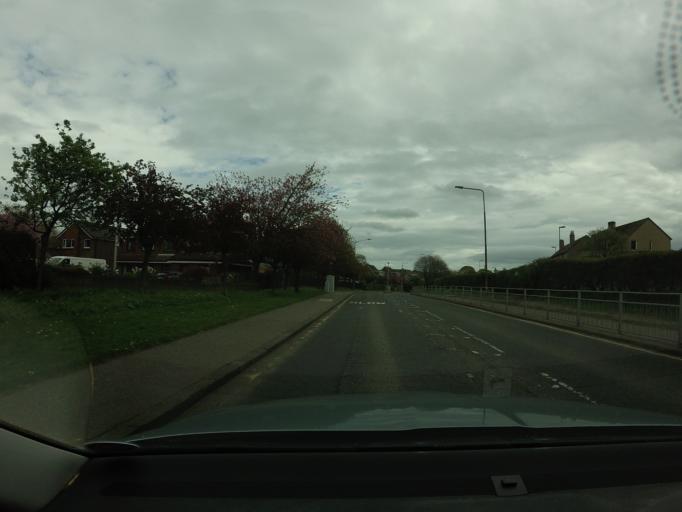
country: GB
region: Scotland
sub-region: Edinburgh
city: Kirkliston
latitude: 55.9566
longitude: -3.4094
